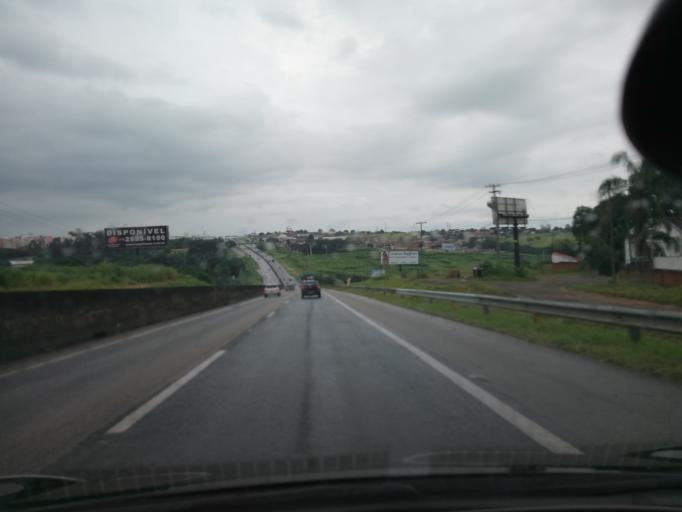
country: BR
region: Sao Paulo
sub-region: Campinas
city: Campinas
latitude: -22.9647
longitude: -47.0994
